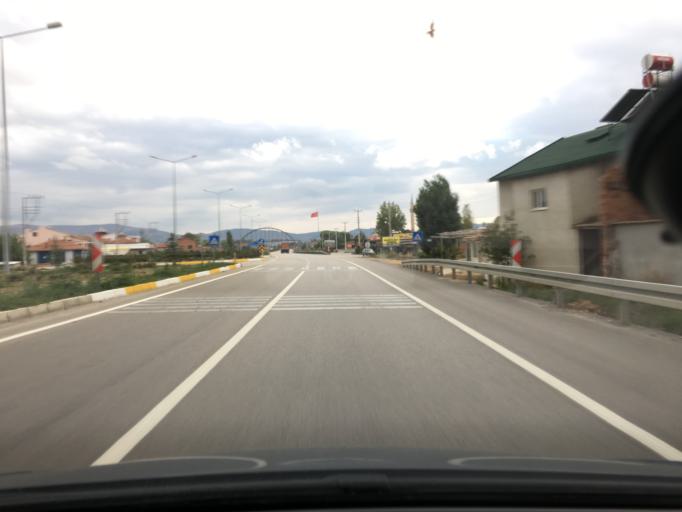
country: TR
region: Afyonkarahisar
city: Sincanli
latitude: 38.7784
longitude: 30.3731
